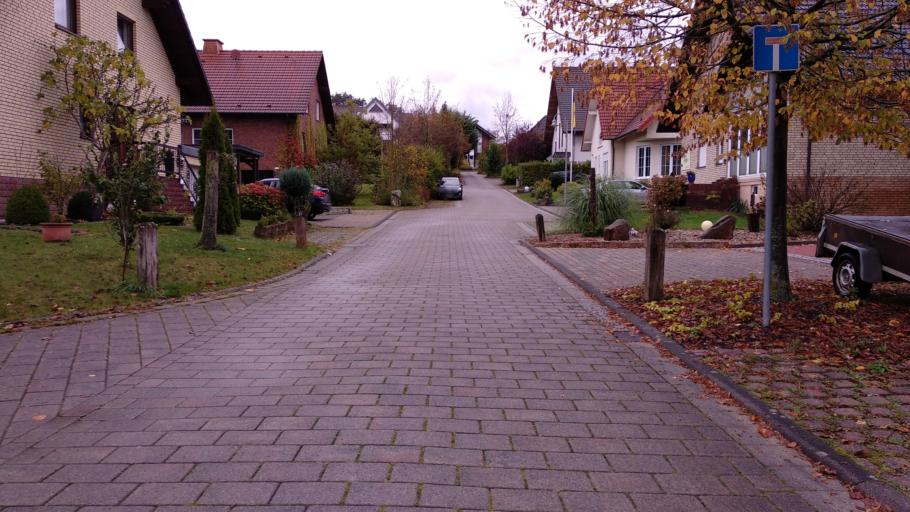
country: DE
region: North Rhine-Westphalia
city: Beverungen
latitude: 51.6615
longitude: 9.3644
